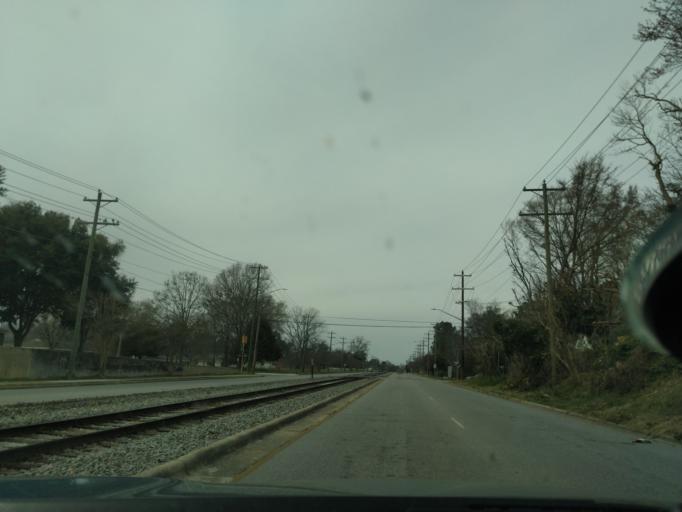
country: US
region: North Carolina
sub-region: Edgecombe County
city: Tarboro
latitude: 35.9006
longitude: -77.5396
